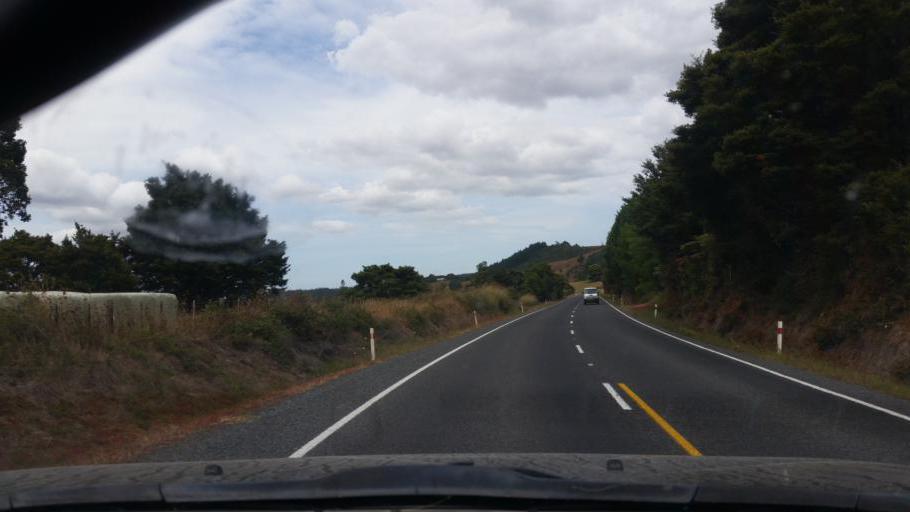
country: NZ
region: Northland
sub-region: Kaipara District
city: Dargaville
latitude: -35.7945
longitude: 173.7275
